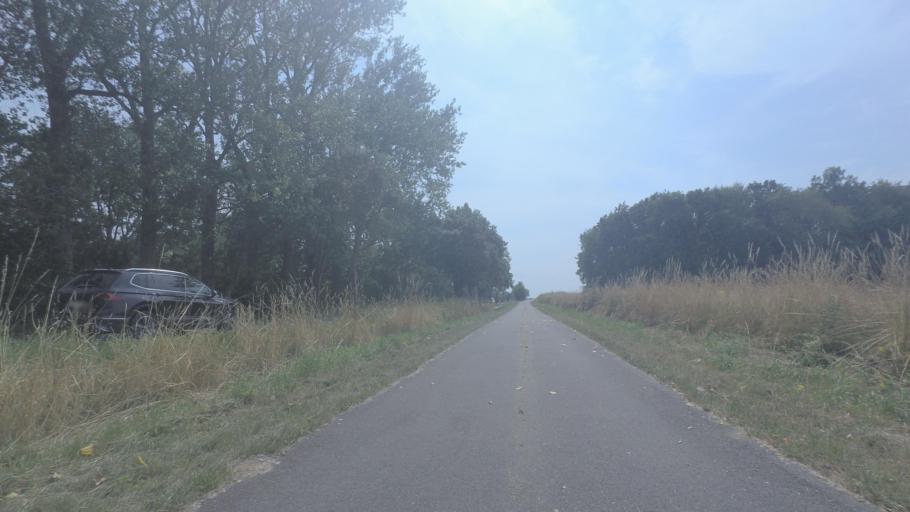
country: DE
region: Mecklenburg-Vorpommern
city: Garz
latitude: 54.2896
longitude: 13.3491
